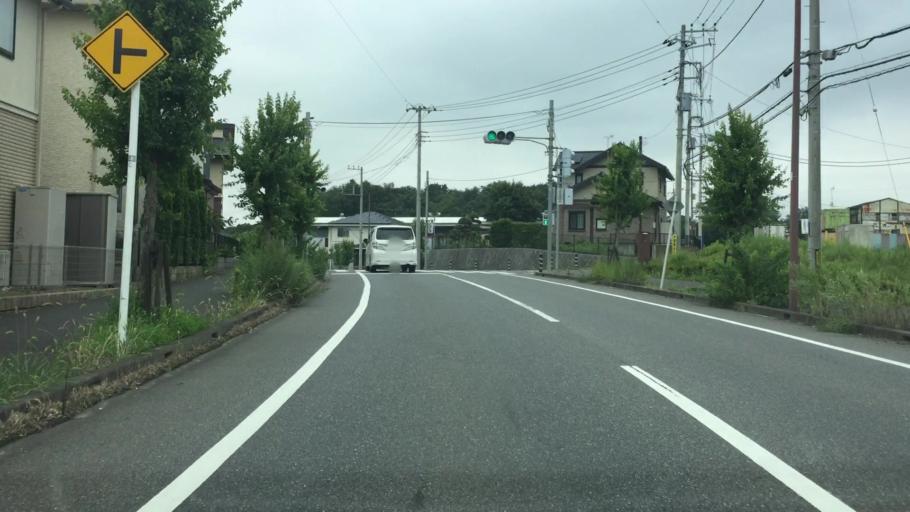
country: JP
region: Chiba
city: Abiko
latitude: 35.8443
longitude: 140.0177
